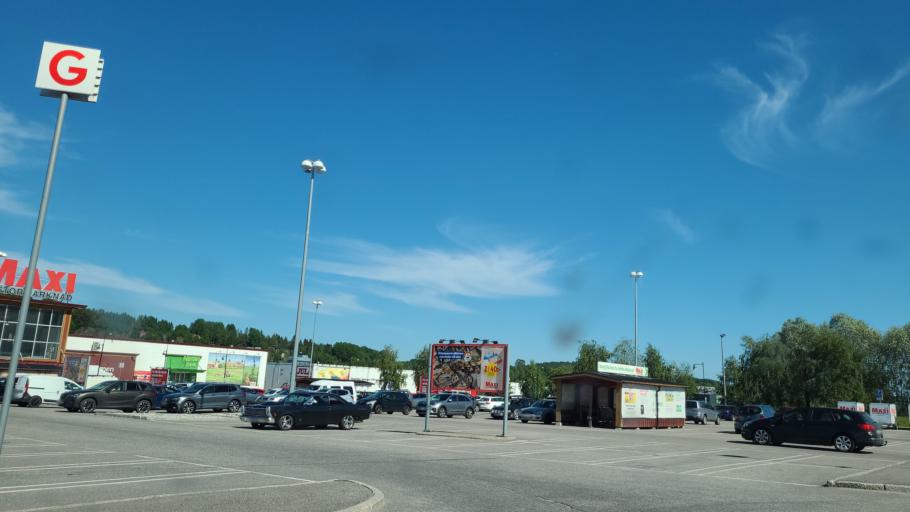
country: SE
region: Vaesternorrland
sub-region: Sundsvalls Kommun
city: Sundsbruk
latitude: 62.4420
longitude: 17.3460
